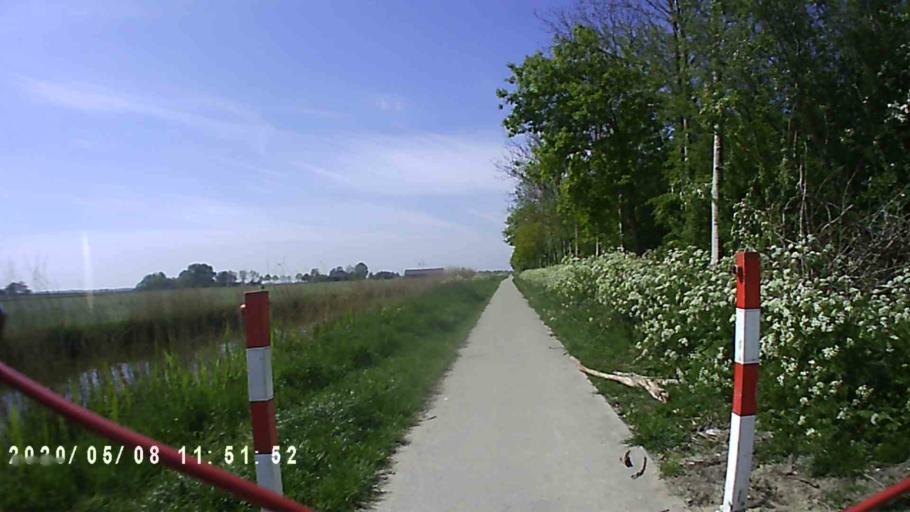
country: NL
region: Groningen
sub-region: Gemeente Bedum
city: Bedum
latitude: 53.3189
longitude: 6.6937
